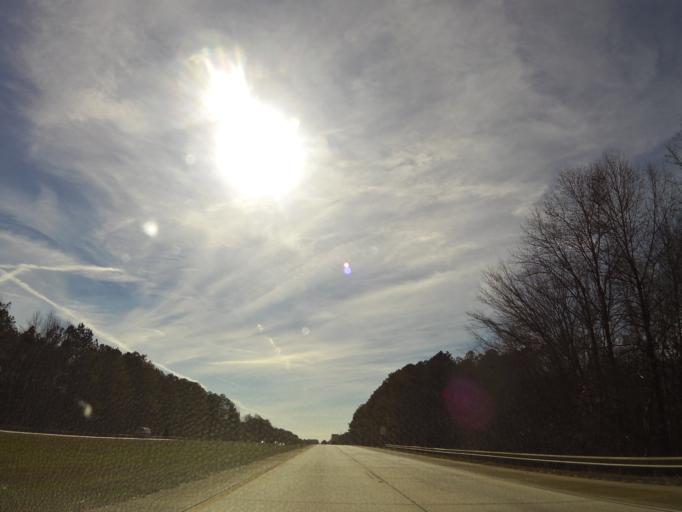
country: US
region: Georgia
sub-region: Coweta County
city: Grantville
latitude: 33.2125
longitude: -84.8246
